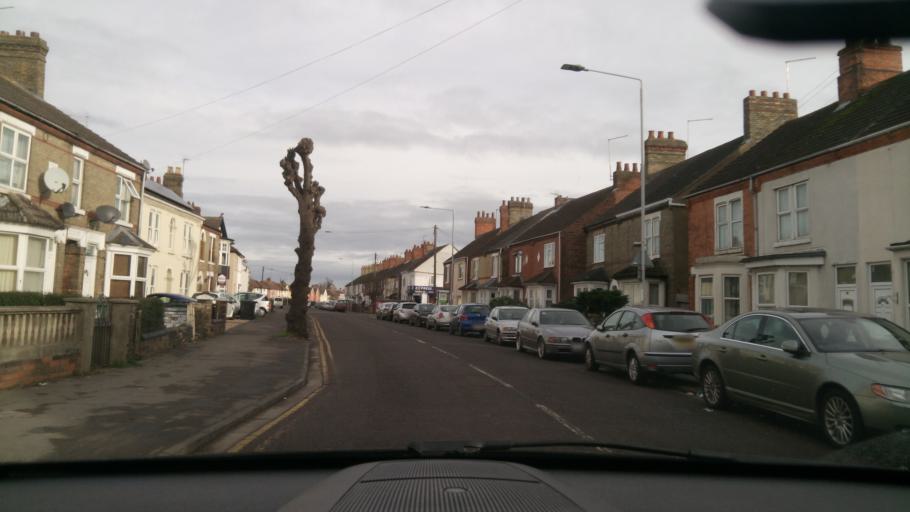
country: GB
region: England
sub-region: Peterborough
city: Peterborough
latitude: 52.5933
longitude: -0.2521
